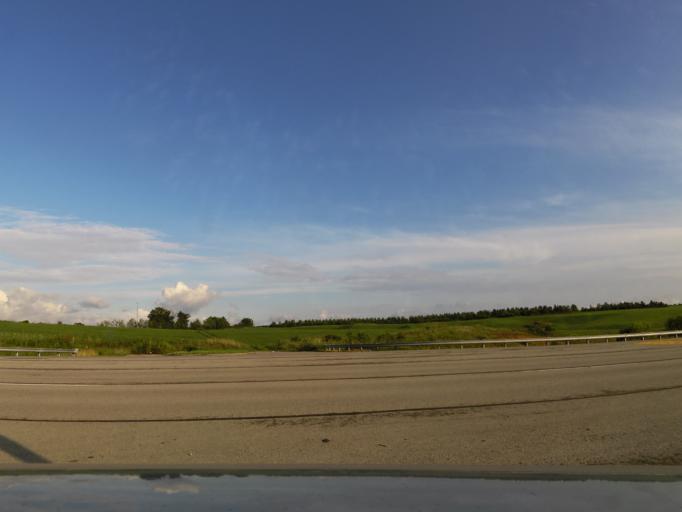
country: US
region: Kentucky
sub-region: Madison County
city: Richmond
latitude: 37.6727
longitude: -84.3156
